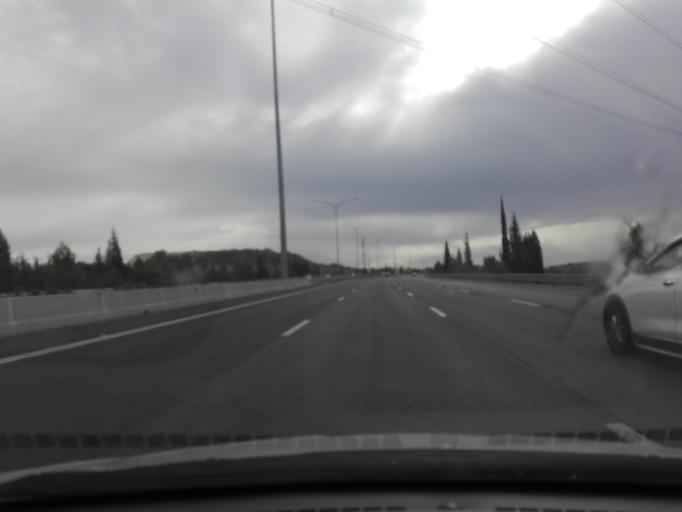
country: PS
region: West Bank
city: Rantis
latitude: 32.0243
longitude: 34.9635
